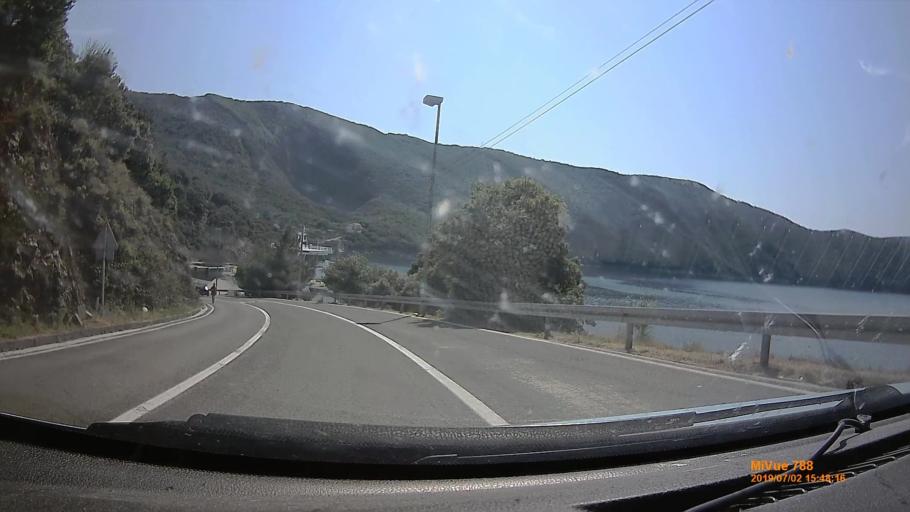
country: HR
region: Primorsko-Goranska
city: Cres
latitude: 44.9813
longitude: 14.4494
